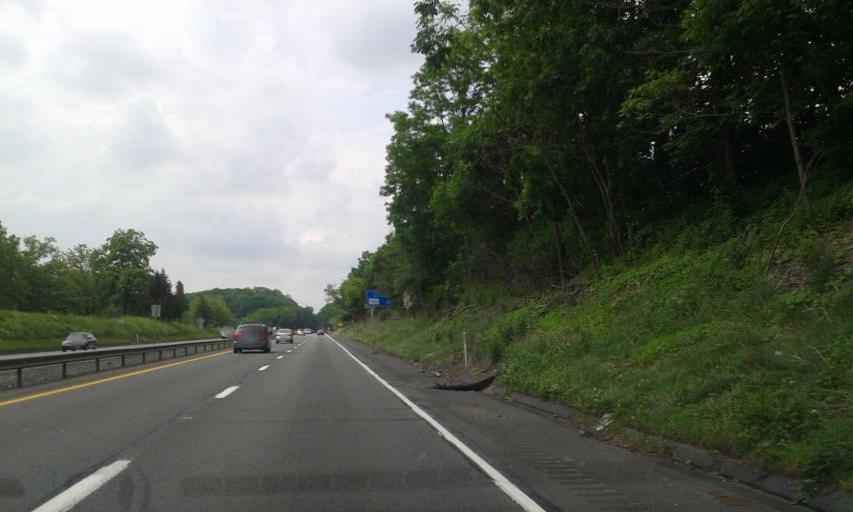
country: US
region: Pennsylvania
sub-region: Monroe County
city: Saylorsburg
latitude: 40.8865
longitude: -75.3097
